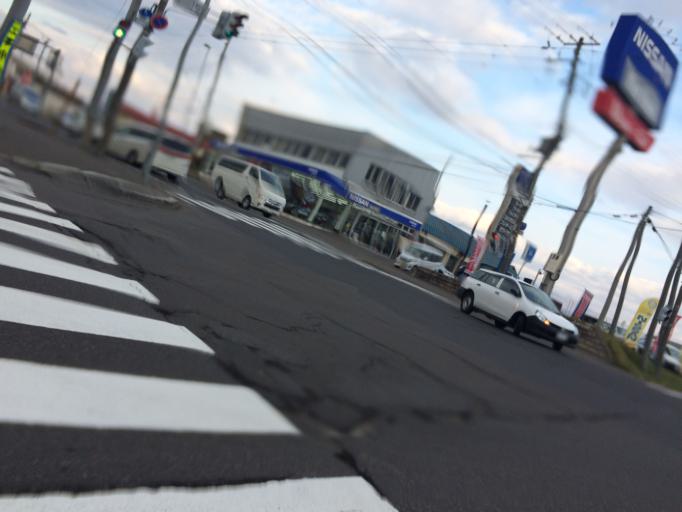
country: JP
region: Hokkaido
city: Niseko Town
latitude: 42.8897
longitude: 140.7513
